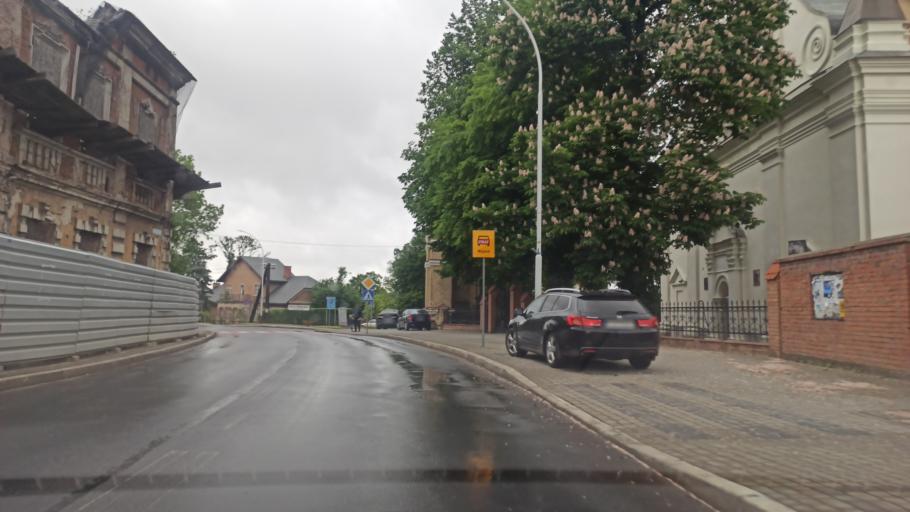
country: PL
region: Subcarpathian Voivodeship
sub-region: Powiat jaroslawski
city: Radymno
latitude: 49.9527
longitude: 22.8175
